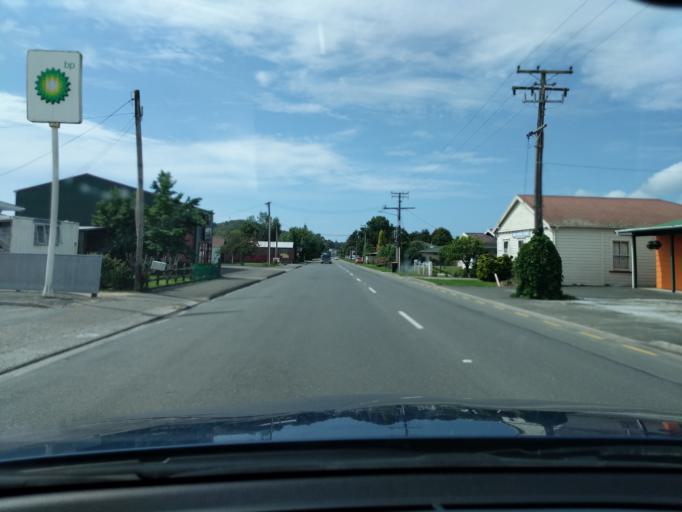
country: NZ
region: Tasman
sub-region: Tasman District
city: Takaka
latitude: -40.8603
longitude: 172.8068
